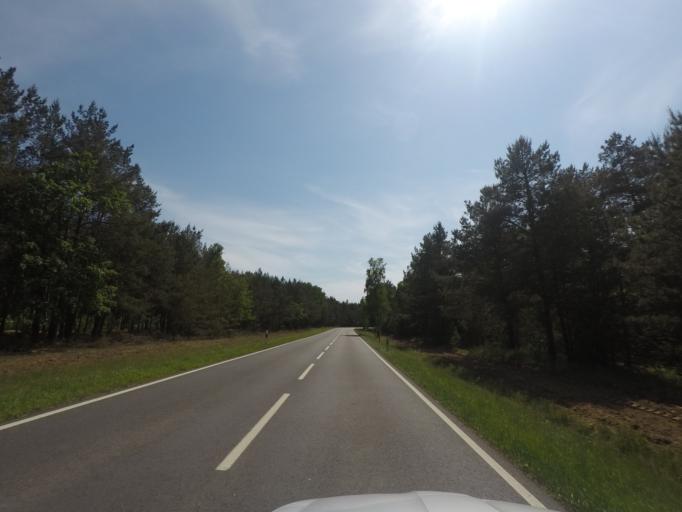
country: DE
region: Brandenburg
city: Britz
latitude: 52.8670
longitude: 13.8075
